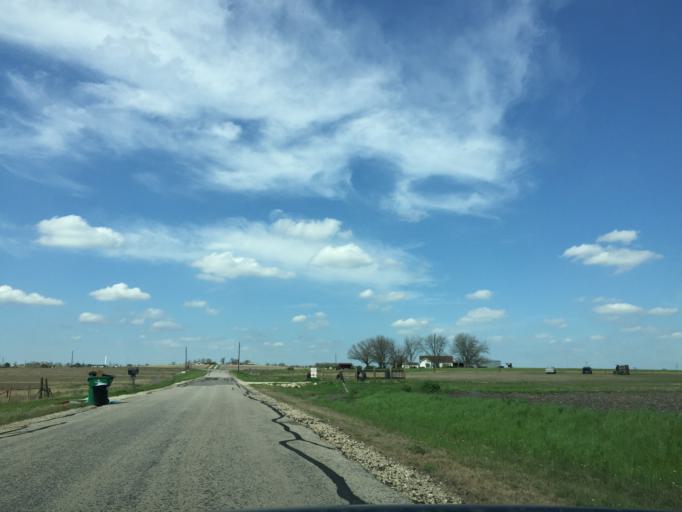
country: US
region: Texas
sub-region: Milam County
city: Thorndale
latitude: 30.5526
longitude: -97.2981
